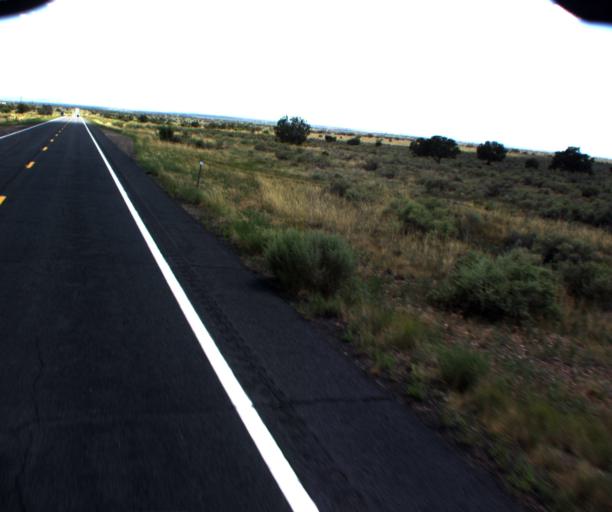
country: US
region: Arizona
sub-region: Coconino County
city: Grand Canyon Village
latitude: 35.7434
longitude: -112.1311
